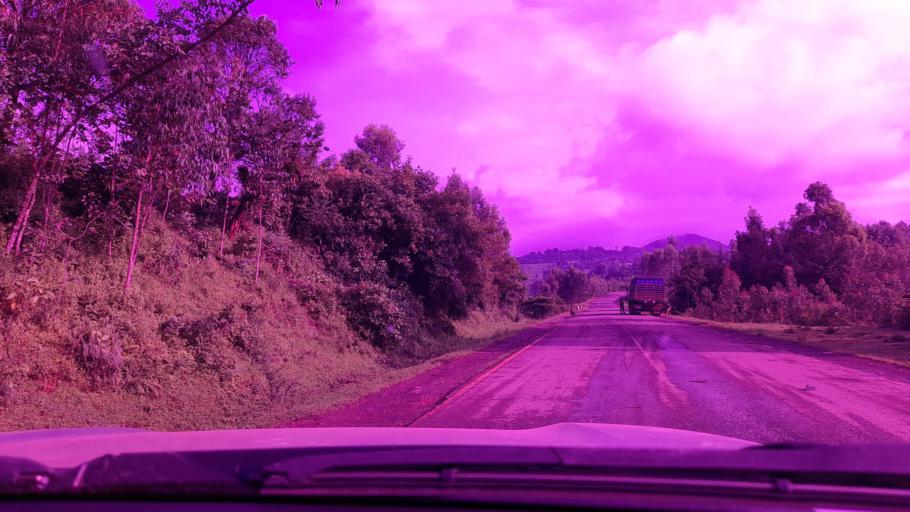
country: ET
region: Oromiya
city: Bedele
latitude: 8.2147
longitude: 36.4451
